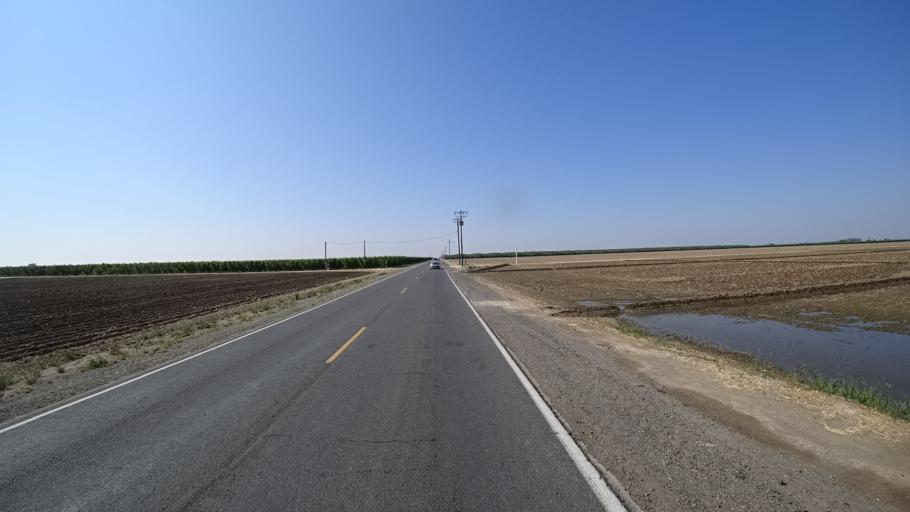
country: US
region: California
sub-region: Kings County
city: Lucerne
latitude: 36.3985
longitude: -119.5650
